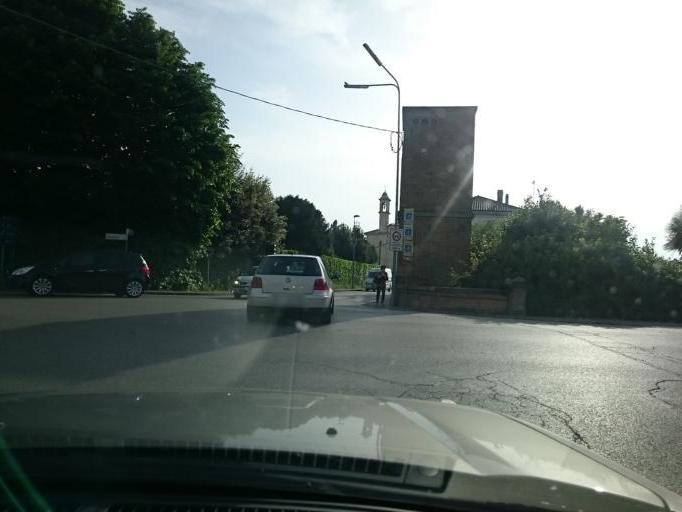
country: IT
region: Veneto
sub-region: Provincia di Venezia
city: Dolo
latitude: 45.4219
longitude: 12.0780
